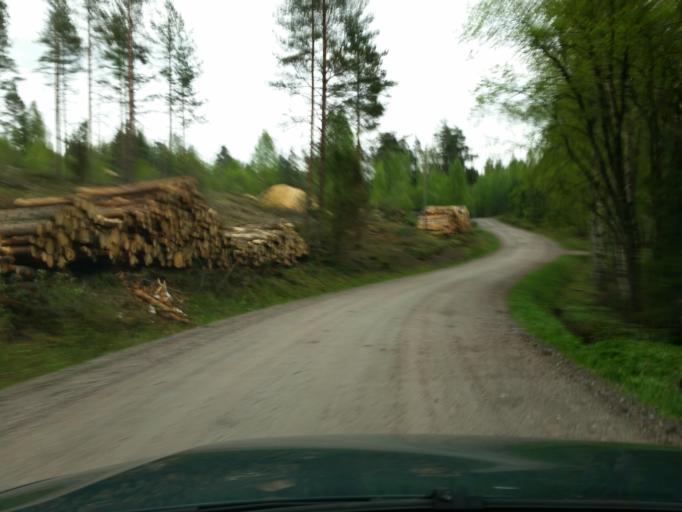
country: FI
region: Uusimaa
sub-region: Helsinki
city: Karjalohja
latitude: 60.1840
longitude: 23.6744
